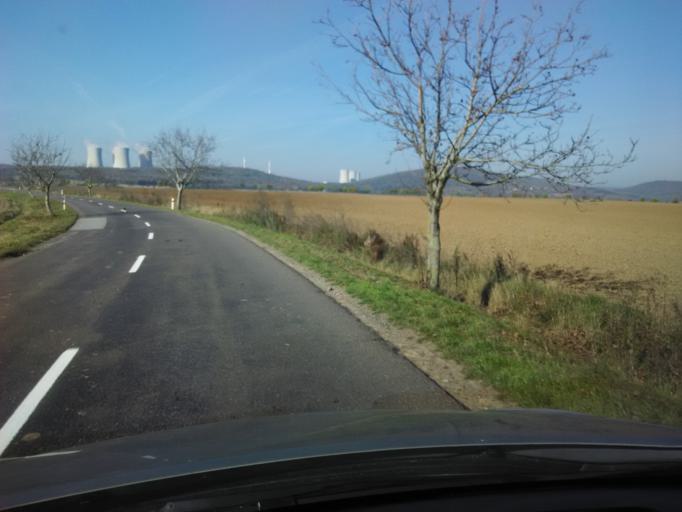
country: SK
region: Nitriansky
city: Tlmace
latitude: 48.2348
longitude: 18.4850
